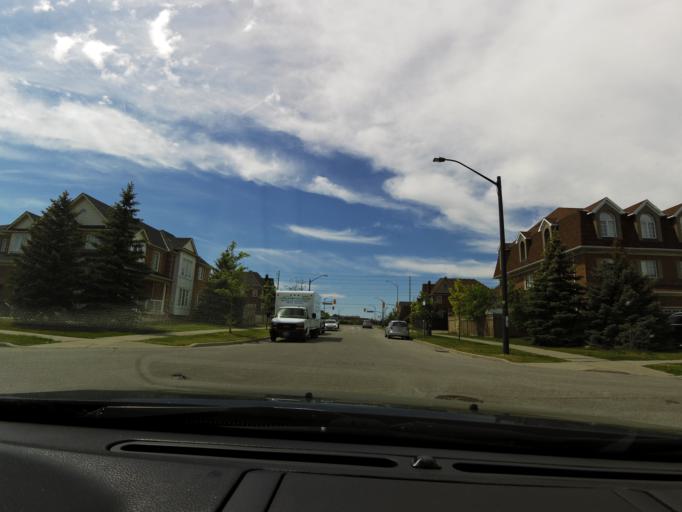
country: CA
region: Ontario
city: Mississauga
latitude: 43.5428
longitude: -79.7228
